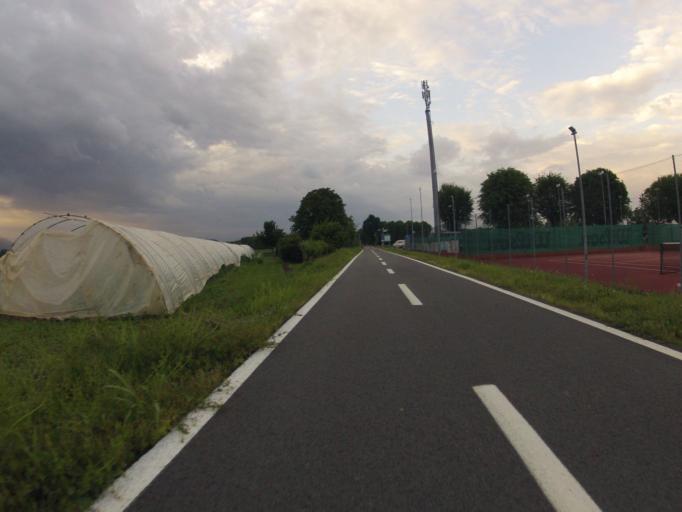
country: IT
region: Piedmont
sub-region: Provincia di Torino
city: Vigone
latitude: 44.8466
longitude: 7.4910
